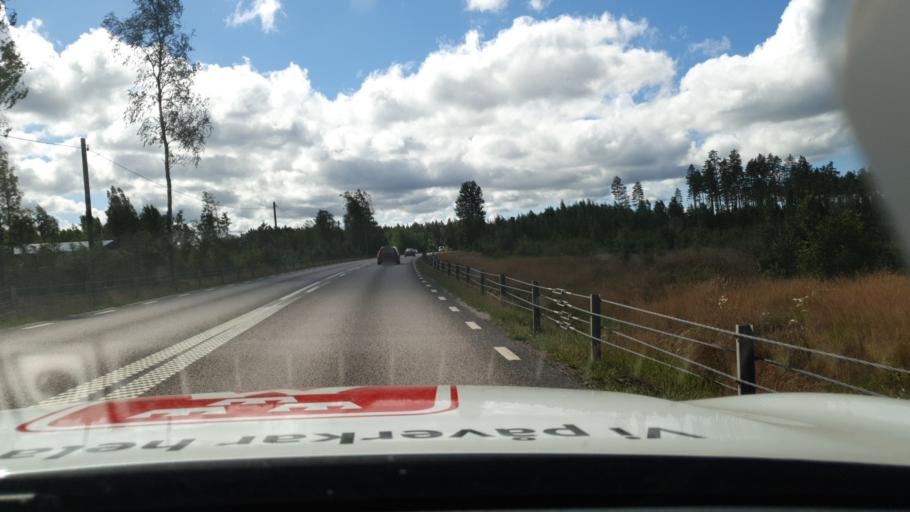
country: SE
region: Vaermland
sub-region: Kristinehamns Kommun
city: Bjorneborg
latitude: 59.2515
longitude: 14.1768
